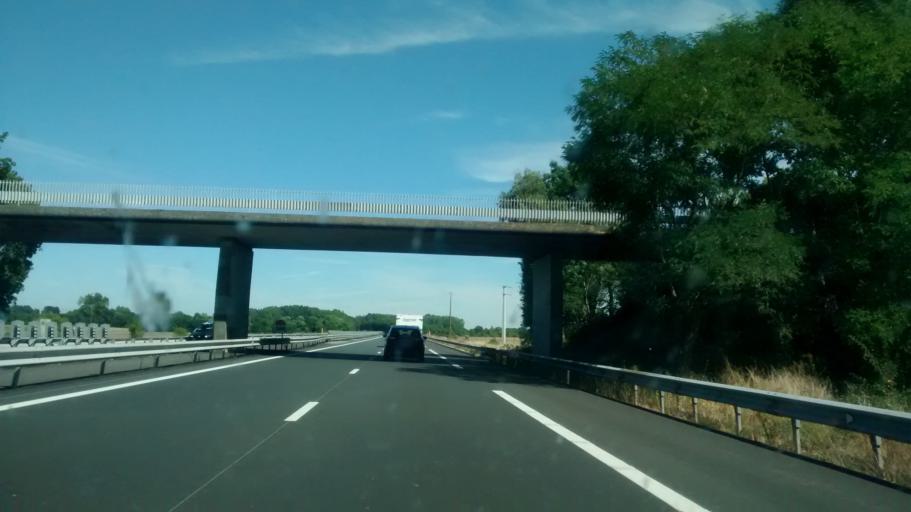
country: FR
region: Poitou-Charentes
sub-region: Departement des Deux-Sevres
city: Beauvoir-sur-Niort
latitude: 46.2069
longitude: -0.4669
